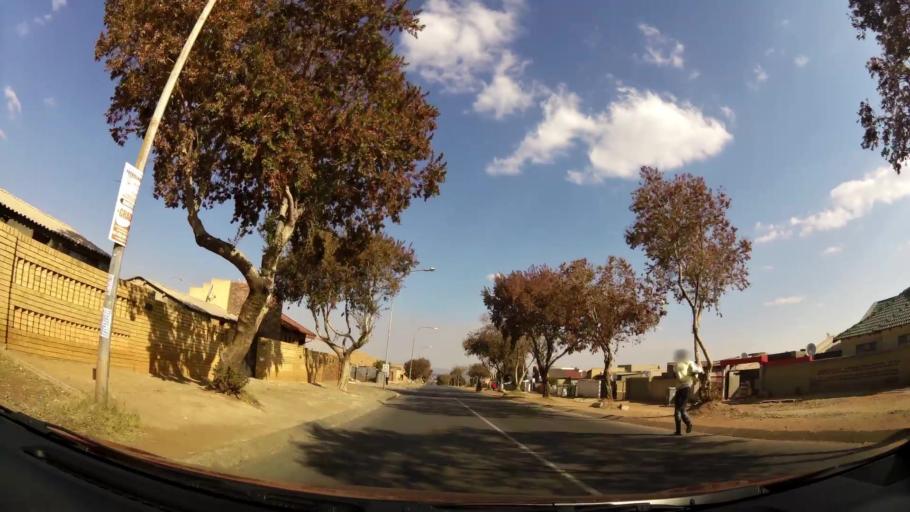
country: ZA
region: Gauteng
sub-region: City of Johannesburg Metropolitan Municipality
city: Roodepoort
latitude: -26.2170
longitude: 27.8900
